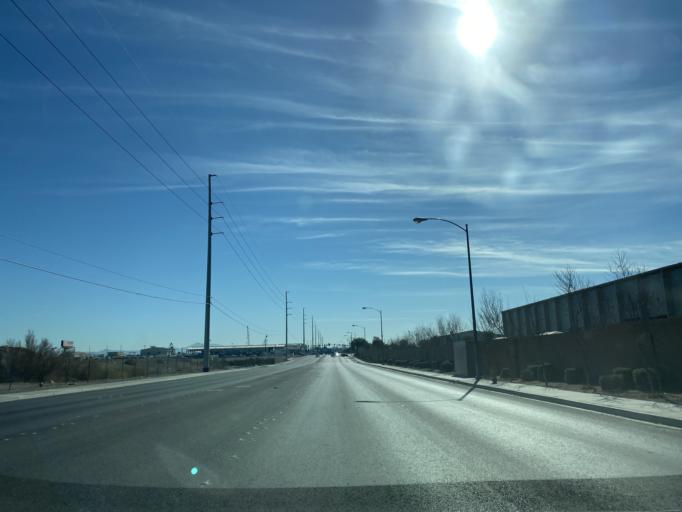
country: US
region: Nevada
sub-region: Clark County
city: North Las Vegas
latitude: 36.2212
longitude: -115.1432
